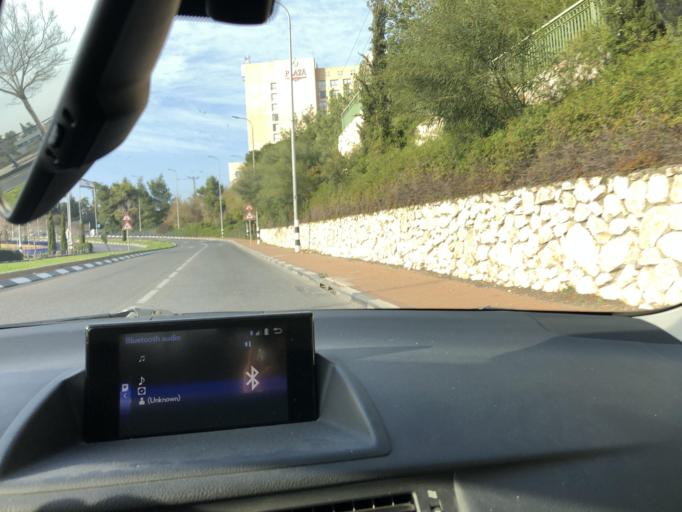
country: IL
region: Northern District
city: Nazareth
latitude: 32.7070
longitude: 35.3134
